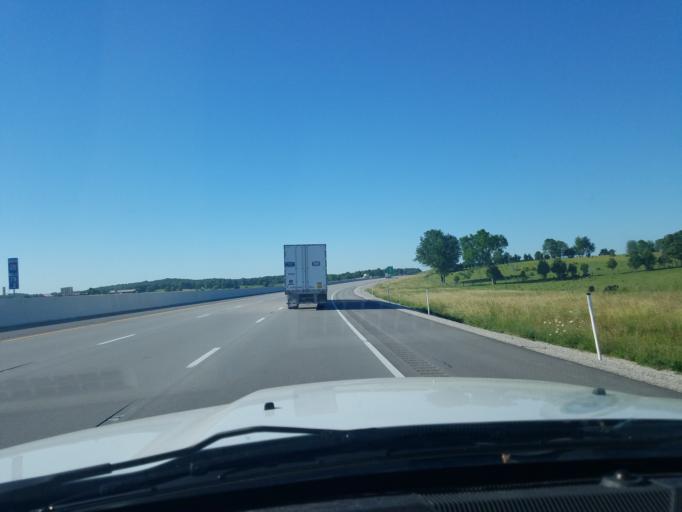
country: US
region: Kentucky
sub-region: Larue County
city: Hodgenville
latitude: 37.4922
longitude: -85.8809
